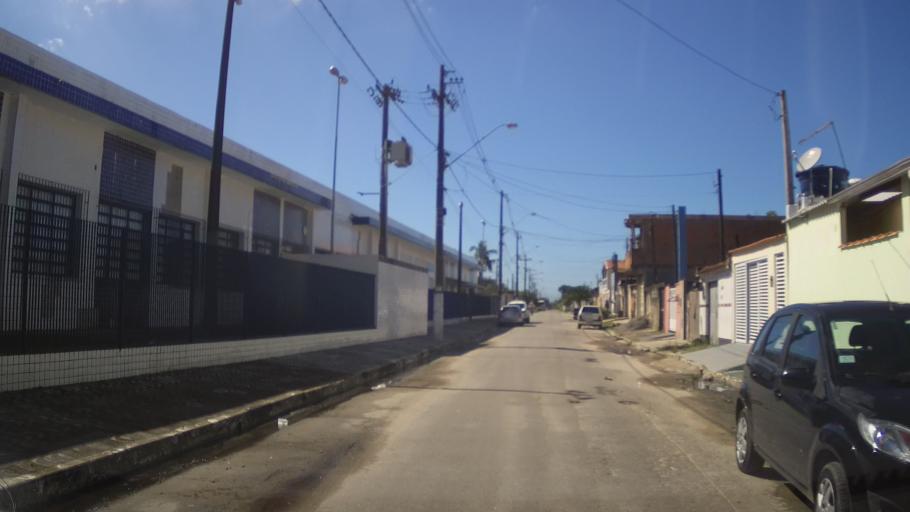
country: BR
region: Sao Paulo
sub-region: Mongagua
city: Mongagua
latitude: -24.0252
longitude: -46.5312
